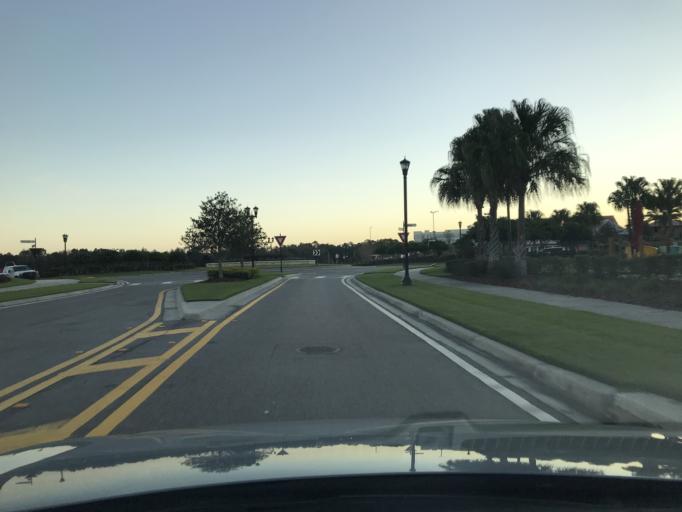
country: US
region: Florida
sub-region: Hillsborough County
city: Pebble Creek
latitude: 28.1959
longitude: -82.3913
